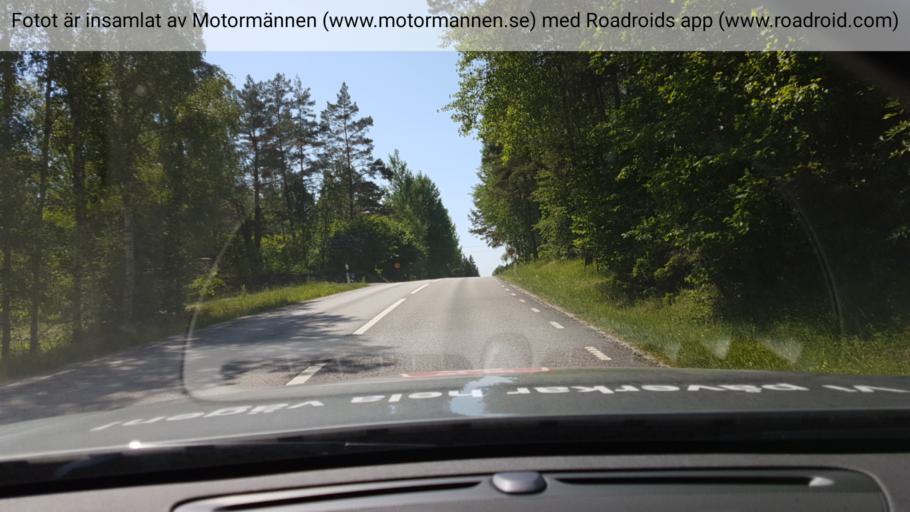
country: SE
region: Stockholm
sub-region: Norrtalje Kommun
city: Rimbo
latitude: 59.6788
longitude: 18.3626
